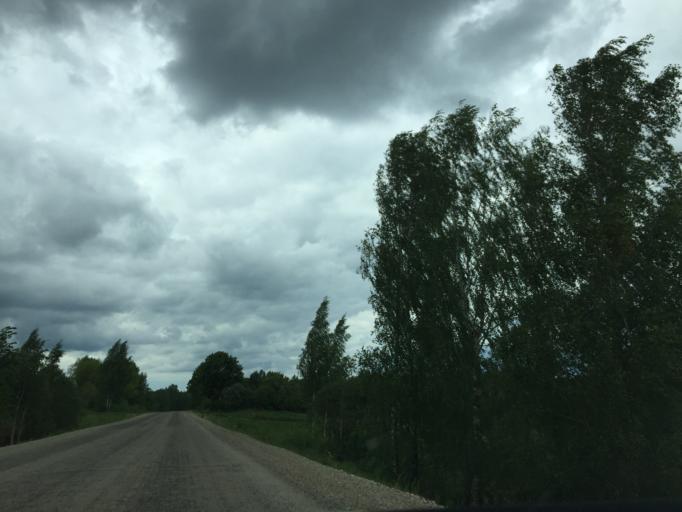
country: LV
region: Dagda
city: Dagda
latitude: 56.0789
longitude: 27.5383
